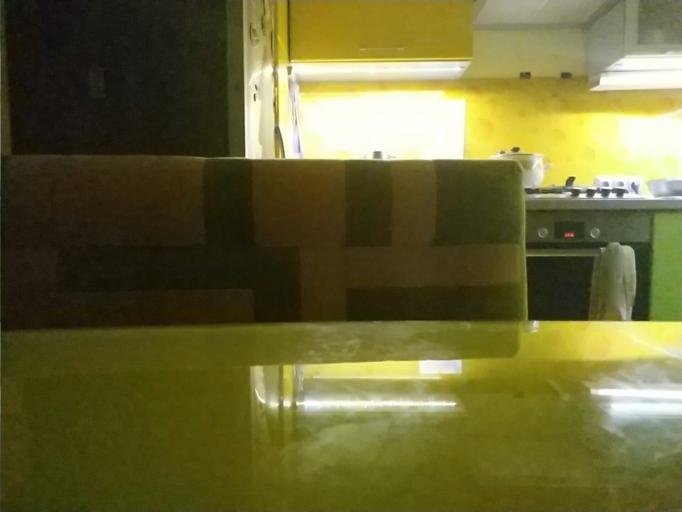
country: RU
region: Republic of Karelia
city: Pyaozerskiy
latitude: 66.0019
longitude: 30.3808
